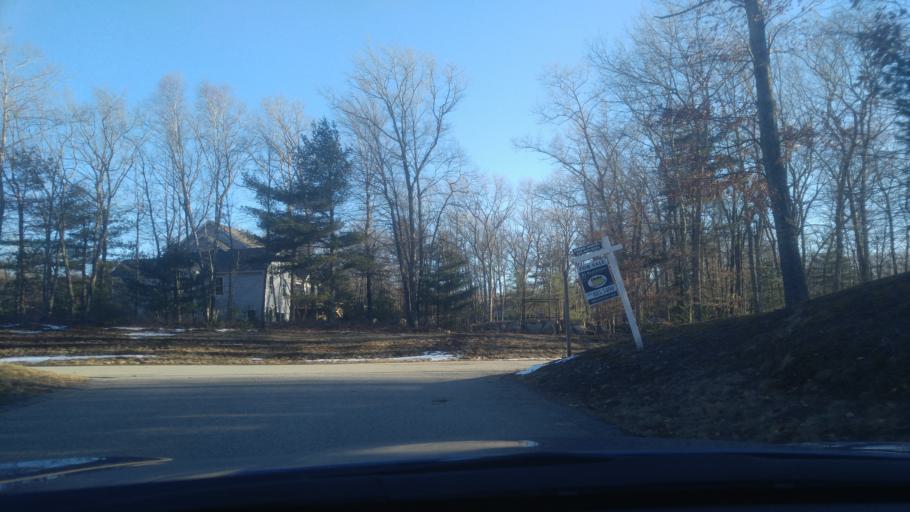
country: US
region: Rhode Island
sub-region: Kent County
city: West Warwick
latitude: 41.6489
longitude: -71.5559
